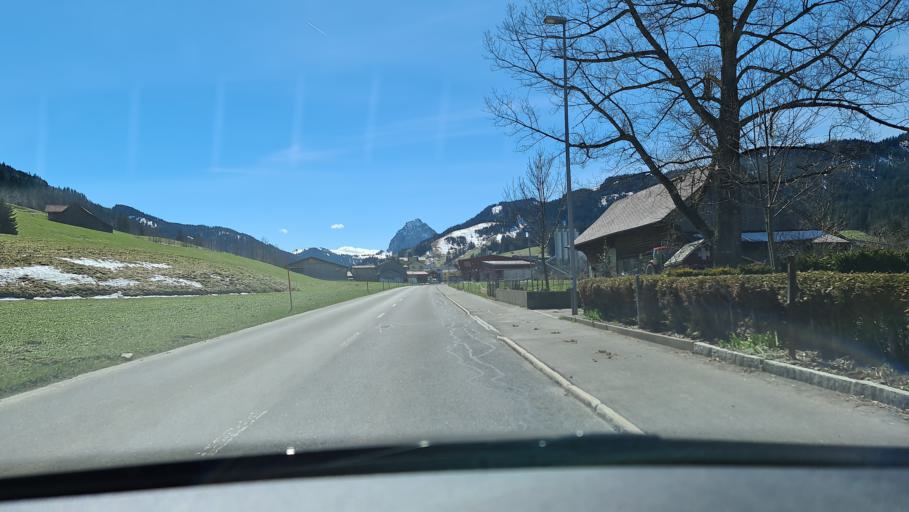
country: CH
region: Schwyz
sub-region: Bezirk Einsiedeln
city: Einsiedeln
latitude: 47.1041
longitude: 8.7300
